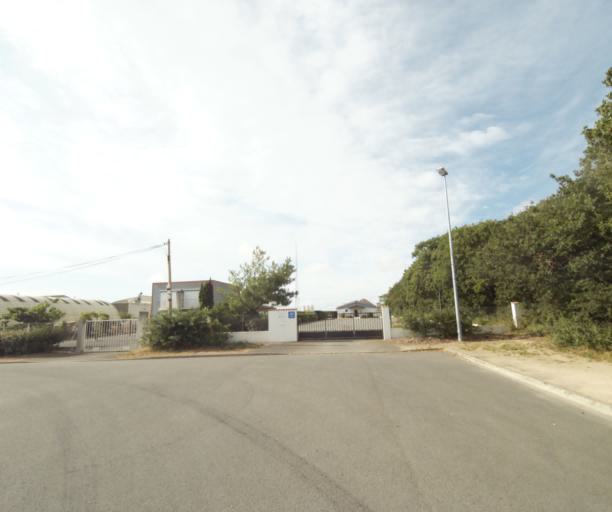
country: FR
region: Pays de la Loire
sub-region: Departement de la Vendee
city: Chateau-d'Olonne
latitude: 46.4896
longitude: -1.7283
